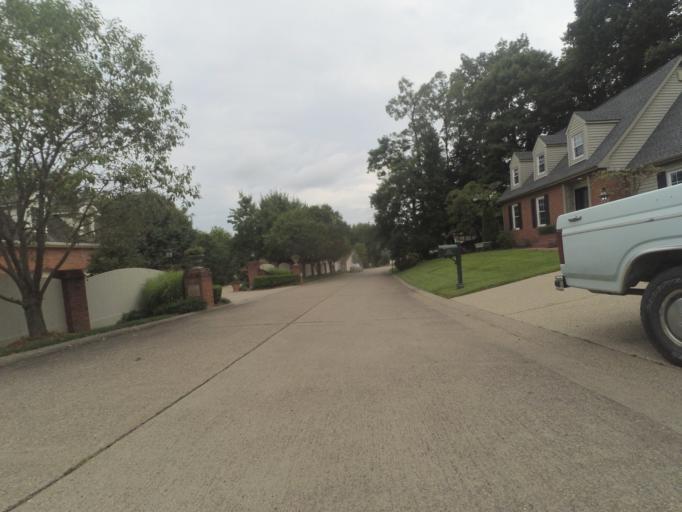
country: US
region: West Virginia
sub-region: Cabell County
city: Huntington
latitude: 38.4006
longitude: -82.3930
